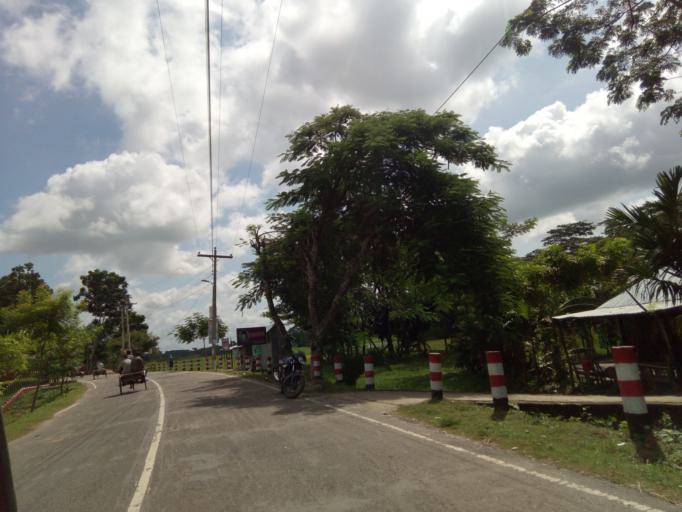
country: BD
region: Dhaka
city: Tungipara
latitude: 22.8977
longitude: 89.8944
